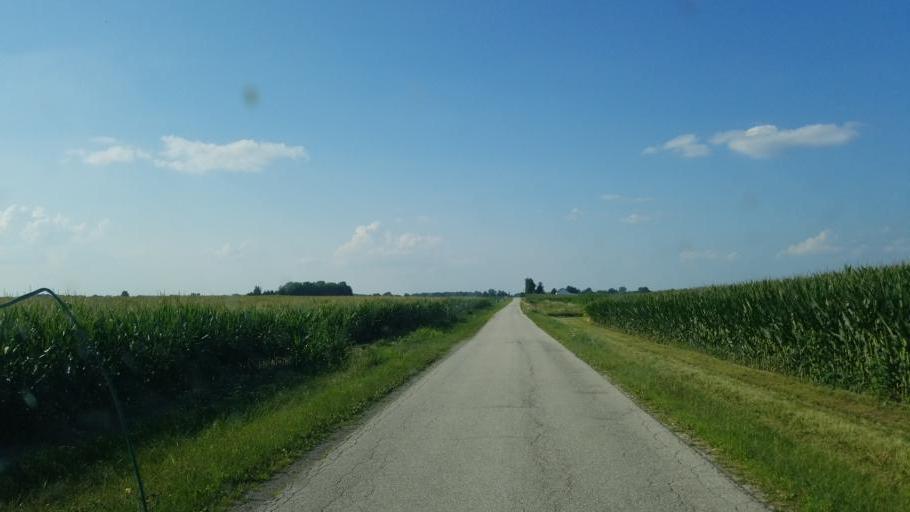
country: US
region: Ohio
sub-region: Crawford County
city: Bucyrus
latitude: 40.7972
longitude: -83.0737
